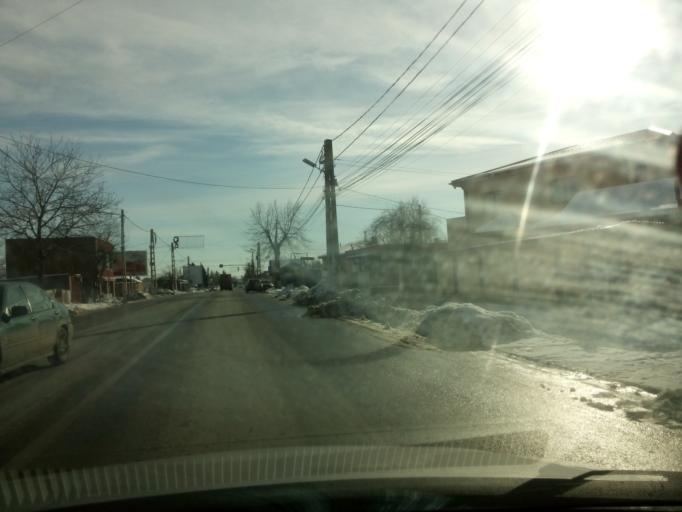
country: RO
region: Ilfov
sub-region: Comuna Popesti-Leordeni
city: Popesti-Leordeni
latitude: 44.3777
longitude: 26.1727
